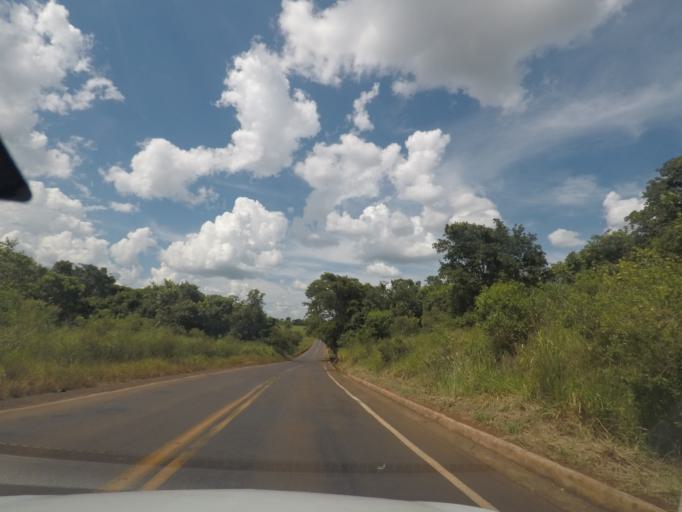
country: BR
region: Minas Gerais
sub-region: Conceicao Das Alagoas
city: Conceicao das Alagoas
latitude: -19.8179
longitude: -48.5903
